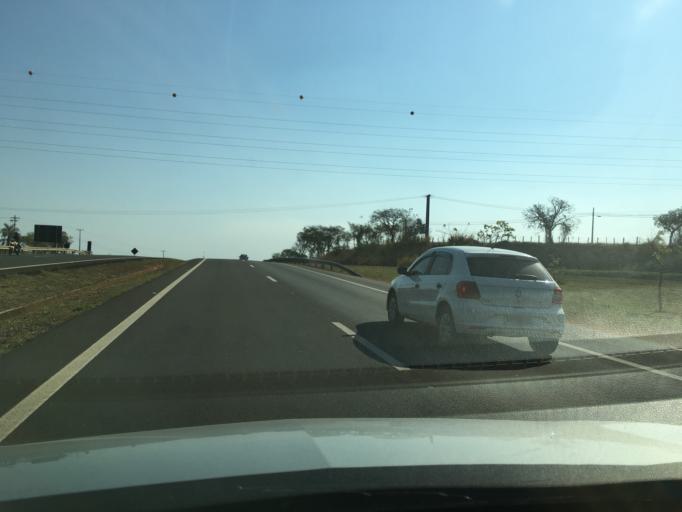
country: BR
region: Sao Paulo
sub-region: Sao Joao Da Boa Vista
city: Sao Joao da Boa Vista
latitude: -21.9955
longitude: -46.8088
